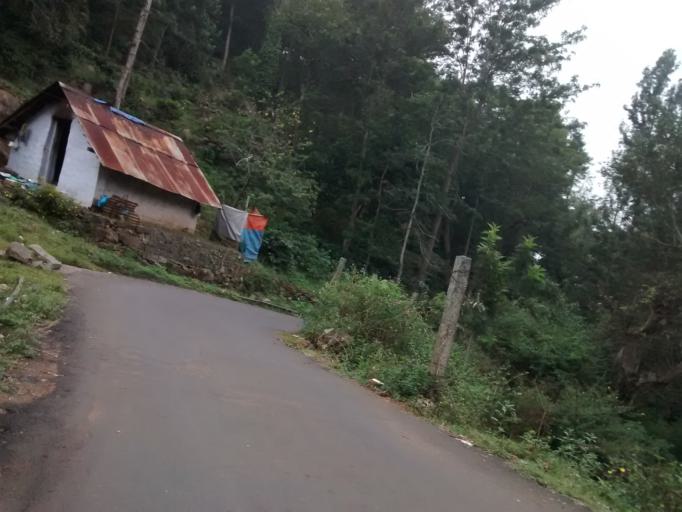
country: IN
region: Tamil Nadu
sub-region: Salem
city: Salem
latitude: 11.7883
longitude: 78.2069
